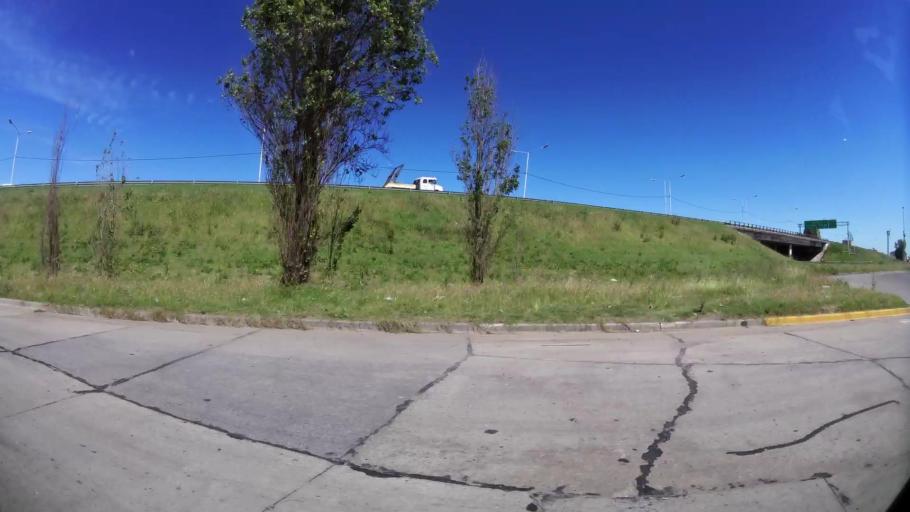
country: AR
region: Santa Fe
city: Perez
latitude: -32.9713
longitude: -60.7159
